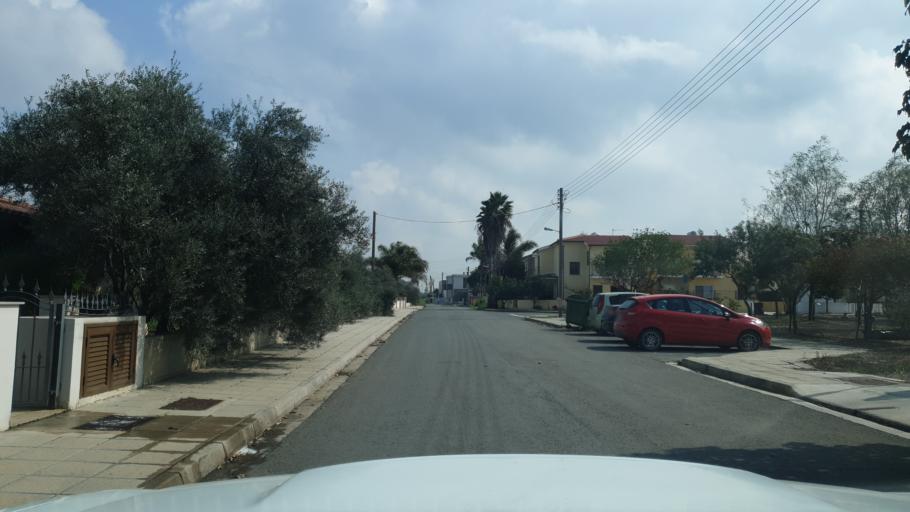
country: CY
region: Lefkosia
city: Kato Deftera
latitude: 35.0884
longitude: 33.2881
